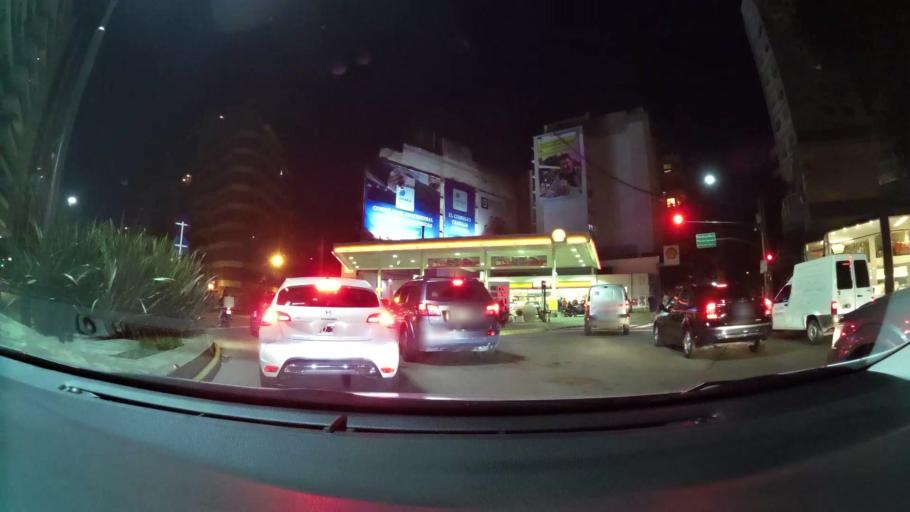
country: AR
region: Buenos Aires F.D.
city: Colegiales
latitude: -34.5691
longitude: -58.4575
